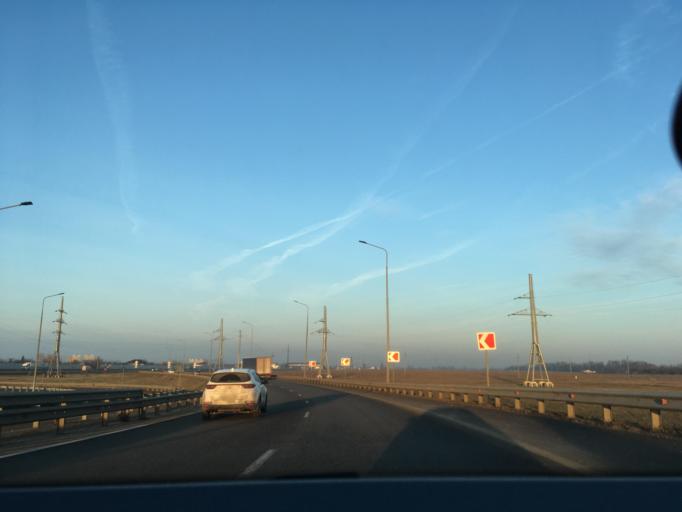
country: RU
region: Krasnodarskiy
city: Agronom
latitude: 45.1795
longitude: 39.1132
